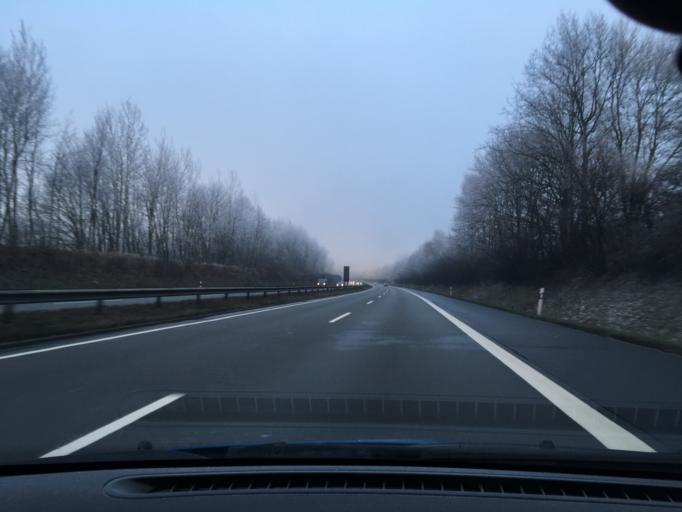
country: DE
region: Lower Saxony
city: Seevetal
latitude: 53.4060
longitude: 9.9127
